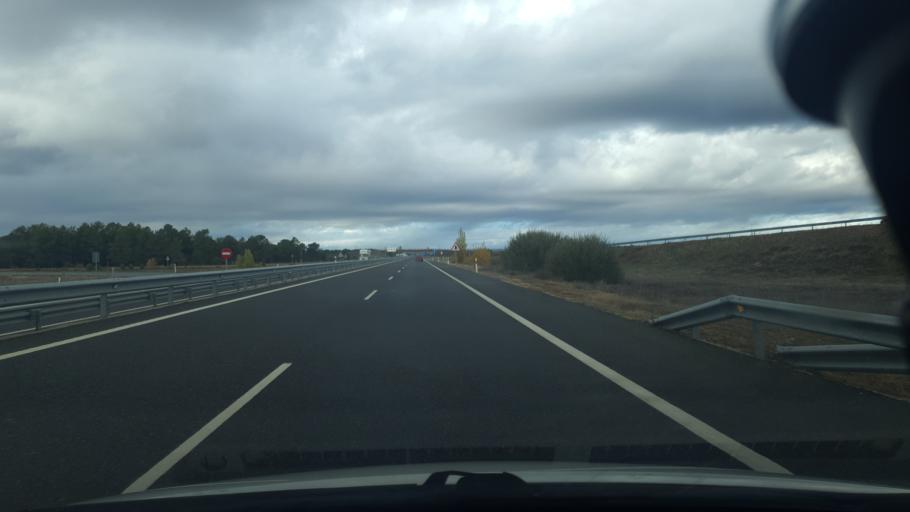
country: ES
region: Castille and Leon
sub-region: Provincia de Segovia
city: Sanchonuno
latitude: 41.2947
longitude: -4.3000
